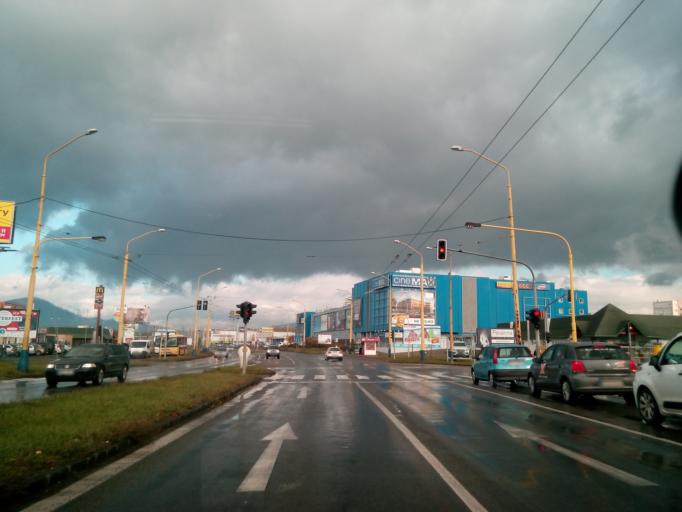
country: SK
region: Presovsky
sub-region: Okres Presov
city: Presov
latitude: 48.9961
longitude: 21.2695
